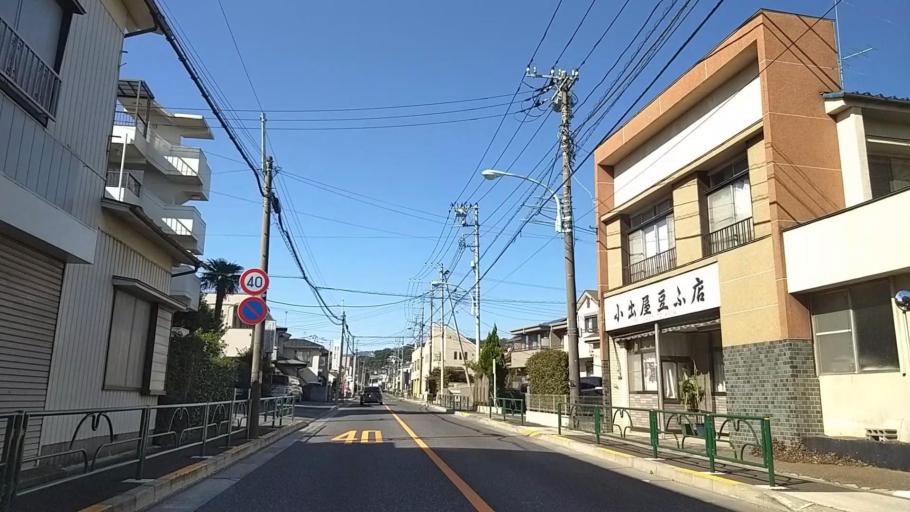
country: JP
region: Tokyo
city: Hachioji
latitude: 35.6048
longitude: 139.3267
